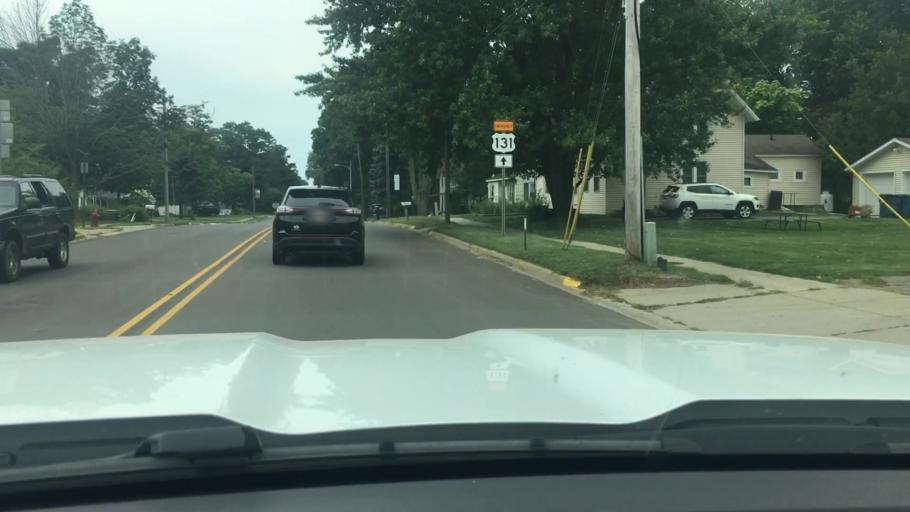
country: US
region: Michigan
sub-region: Allegan County
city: Otsego
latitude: 42.5373
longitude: -85.6424
